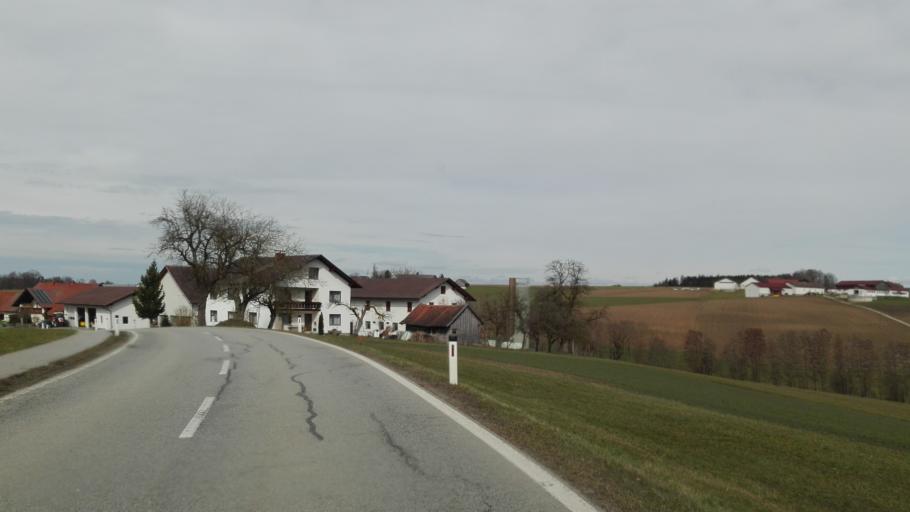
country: DE
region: Bavaria
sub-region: Lower Bavaria
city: Passau
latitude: 48.5429
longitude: 13.4812
